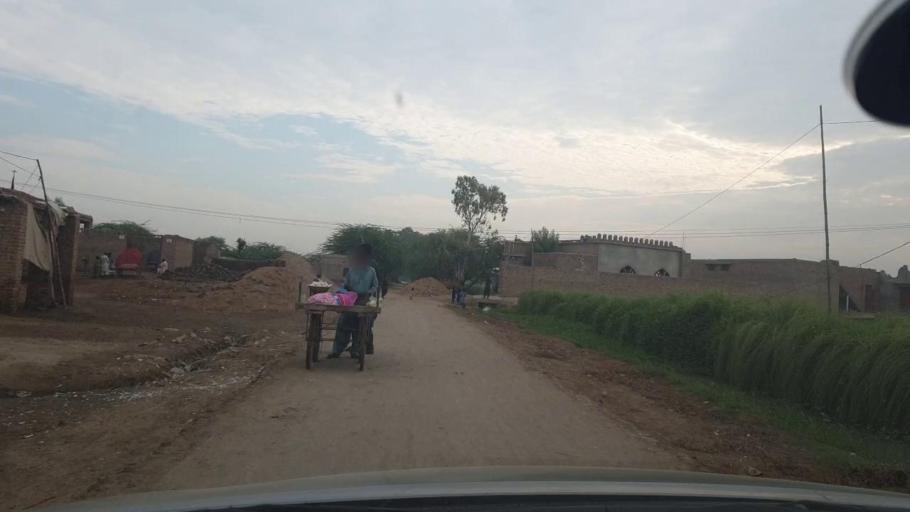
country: PK
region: Sindh
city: Jacobabad
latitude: 28.2935
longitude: 68.4204
